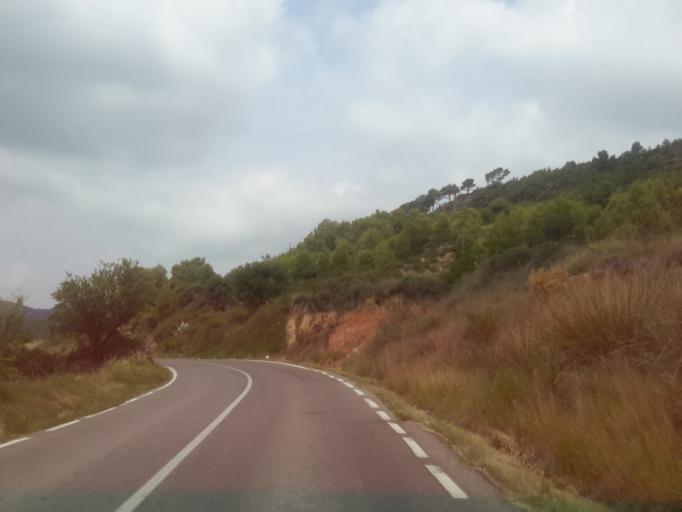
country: ES
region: Catalonia
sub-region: Provincia de Barcelona
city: Sant Marti Sarroca
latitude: 41.3917
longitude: 1.5624
